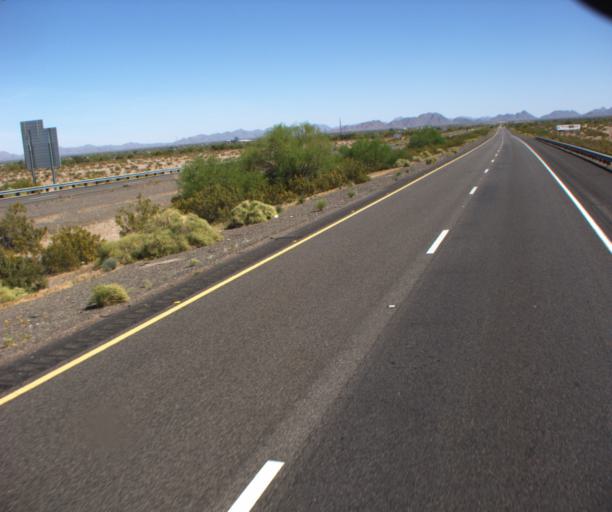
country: US
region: Arizona
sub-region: Maricopa County
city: Gila Bend
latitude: 32.9346
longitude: -112.7144
